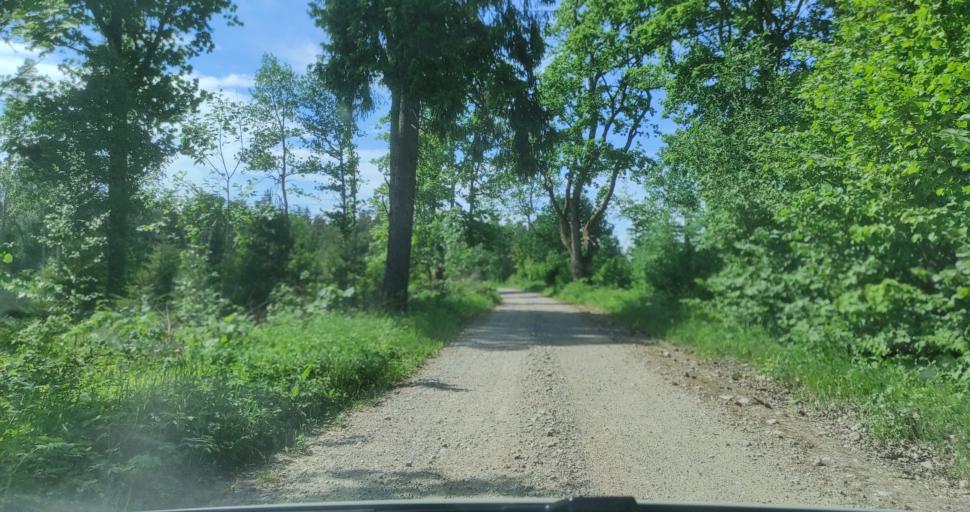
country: LV
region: Kuldigas Rajons
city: Kuldiga
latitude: 56.8483
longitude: 21.9217
